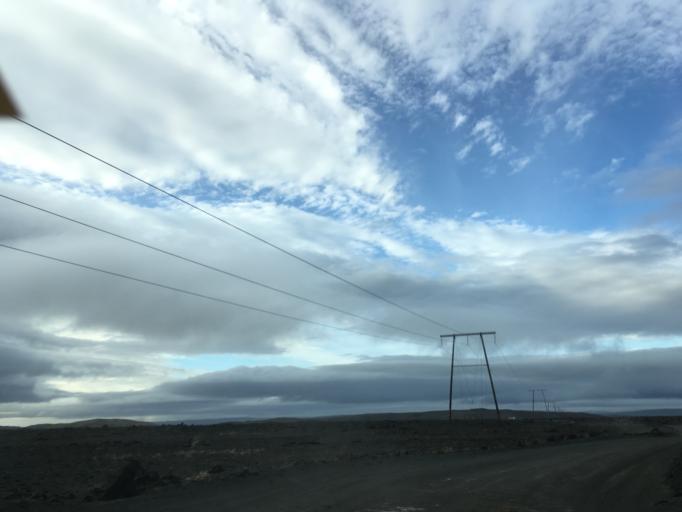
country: IS
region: South
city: Vestmannaeyjar
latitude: 64.1303
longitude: -19.1222
